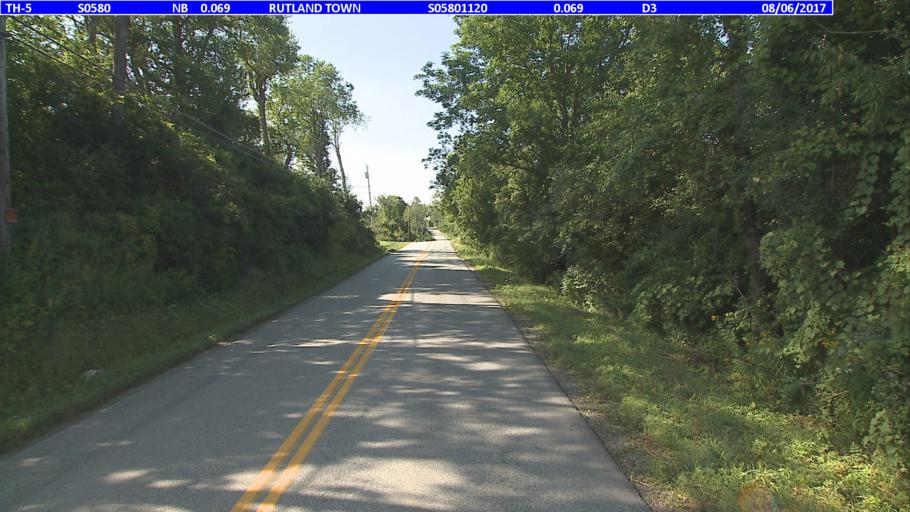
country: US
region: Vermont
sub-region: Rutland County
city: Rutland
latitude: 43.5851
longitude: -72.9517
